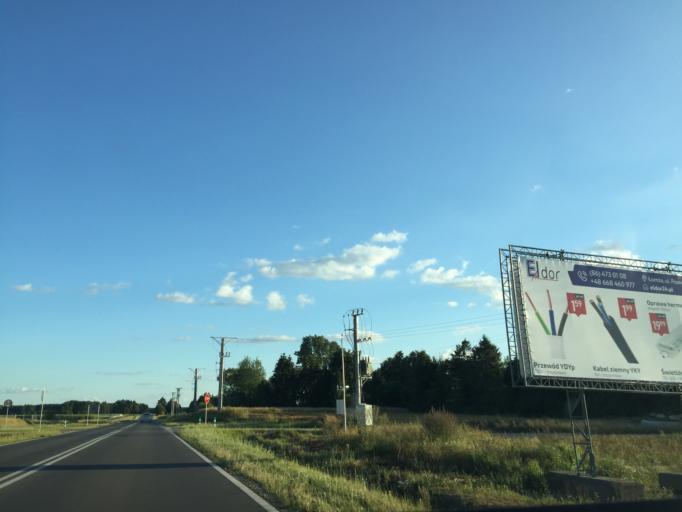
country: PL
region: Podlasie
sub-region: Lomza
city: Lomza
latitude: 53.1376
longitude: 22.0509
